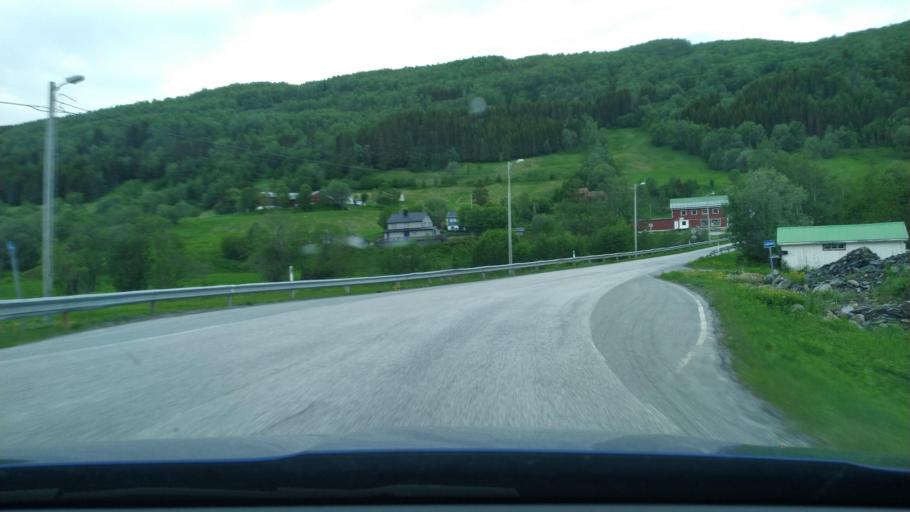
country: NO
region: Troms
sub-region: Sorreisa
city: Sorreisa
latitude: 69.1305
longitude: 18.0543
